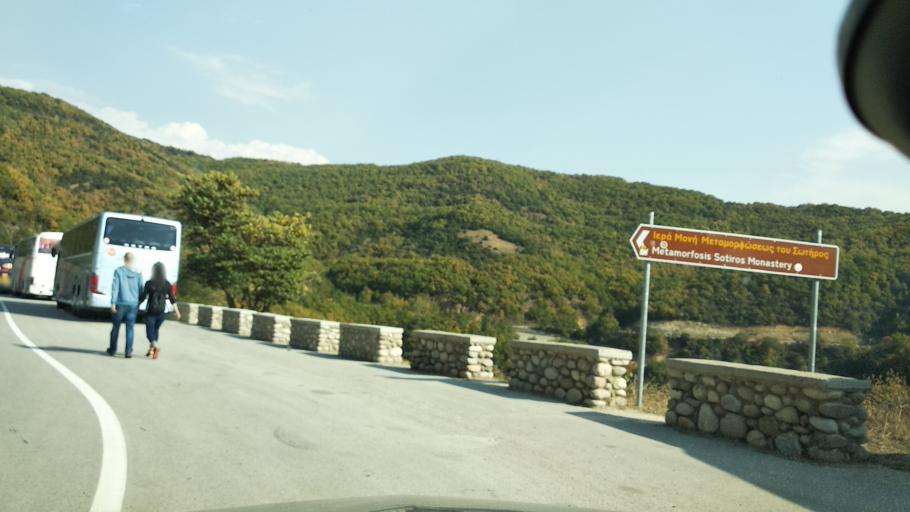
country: GR
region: Thessaly
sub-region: Trikala
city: Kastraki
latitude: 39.7259
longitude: 21.6326
